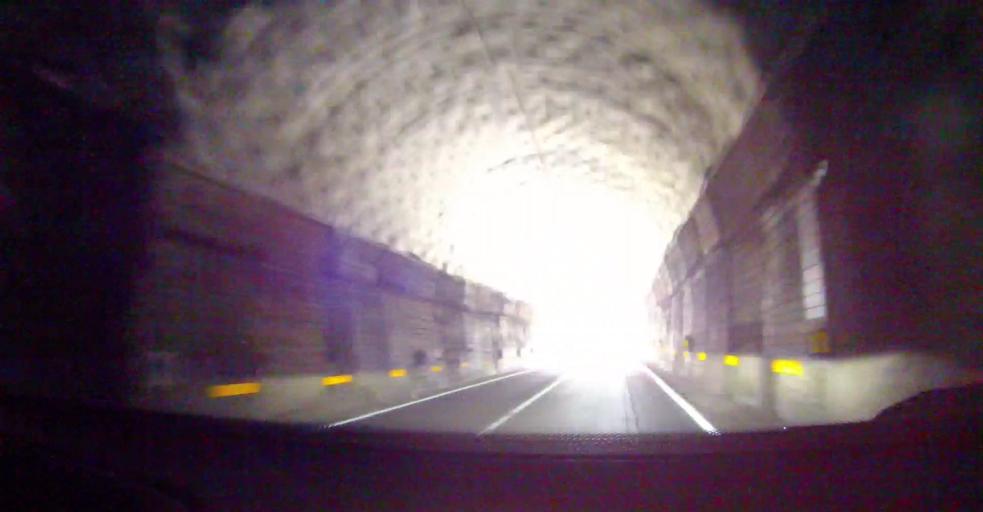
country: ES
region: Castille and Leon
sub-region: Provincia de Leon
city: Puebla de Lillo
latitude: 42.9609
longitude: -5.2529
